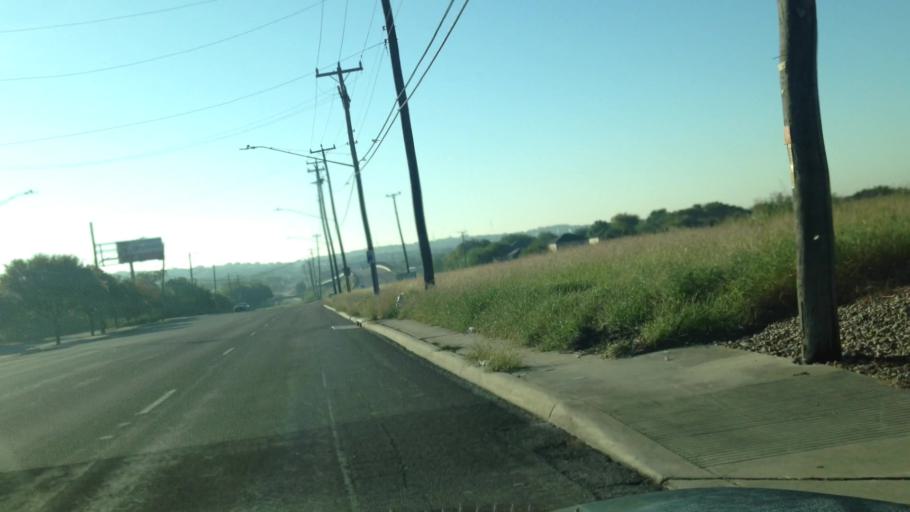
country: US
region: Texas
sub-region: Bexar County
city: Live Oak
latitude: 29.5714
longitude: -98.3683
